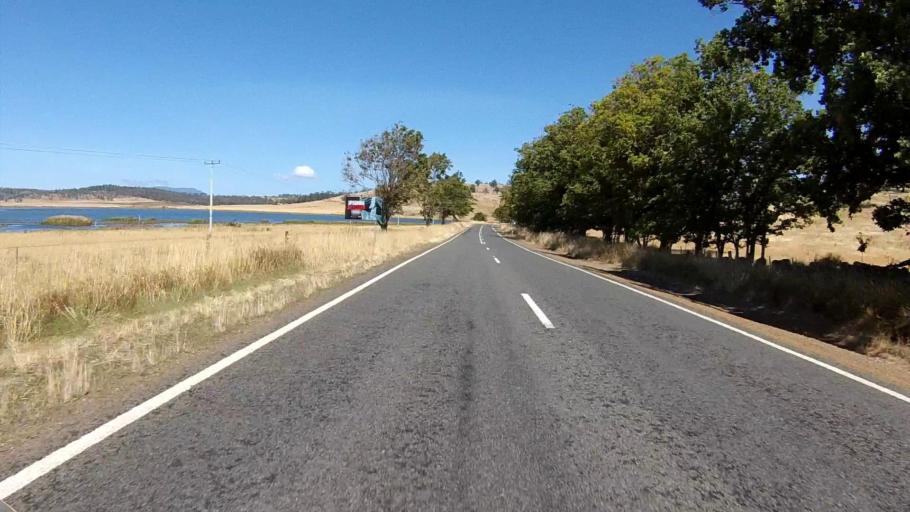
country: AU
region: Tasmania
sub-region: Sorell
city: Sorell
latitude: -42.4853
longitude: 147.9342
